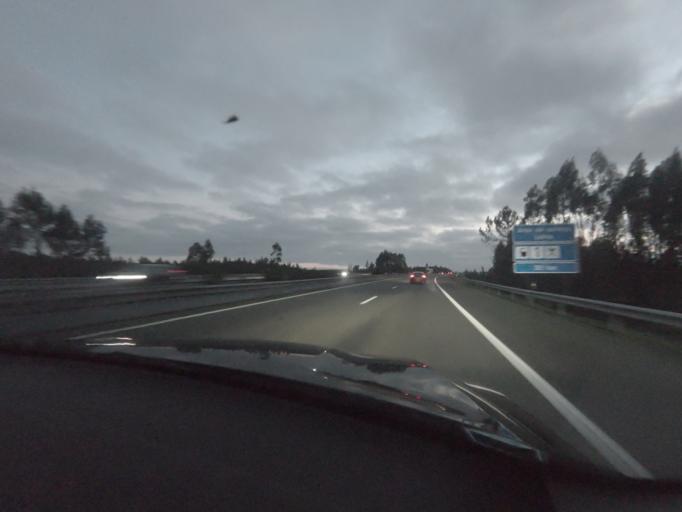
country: PT
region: Leiria
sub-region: Pombal
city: Pombal
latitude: 39.9505
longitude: -8.6700
